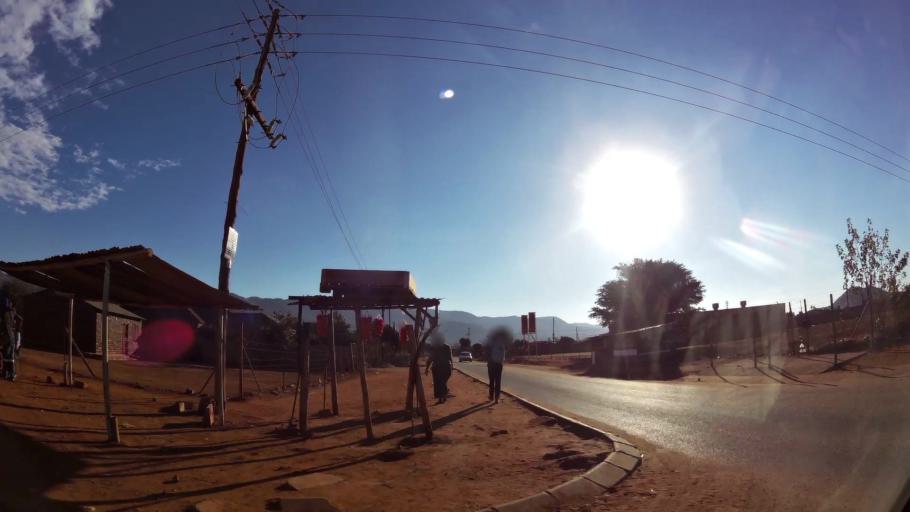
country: ZA
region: Limpopo
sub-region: Waterberg District Municipality
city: Mokopane
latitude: -24.1805
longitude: 28.9833
